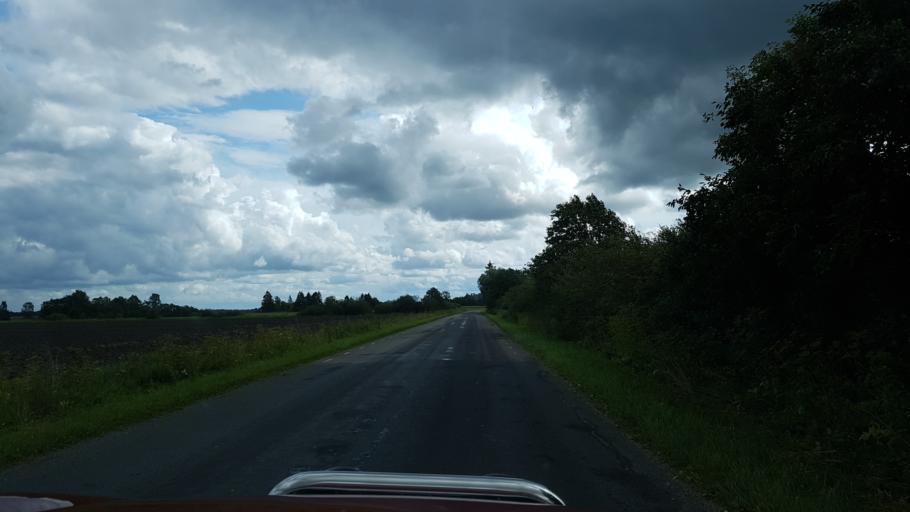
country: EE
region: Laeaene
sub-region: Lihula vald
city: Lihula
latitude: 58.7170
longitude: 23.9901
